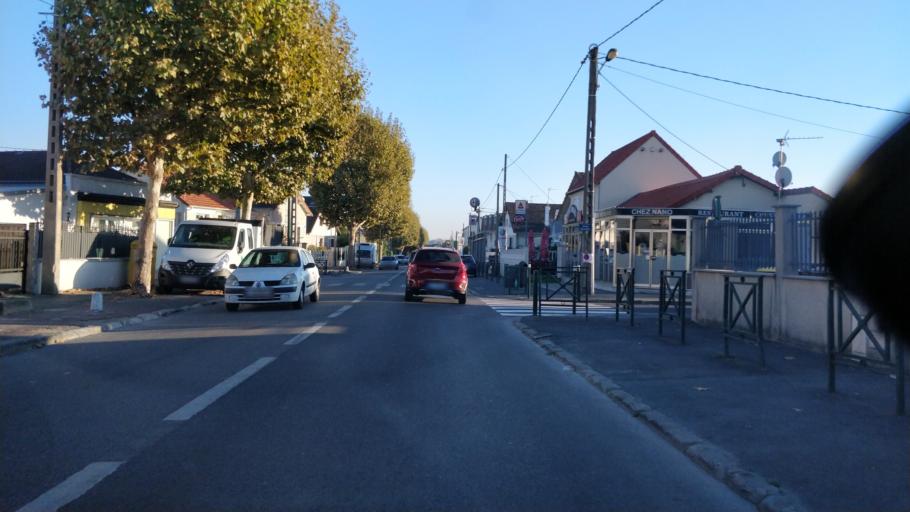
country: FR
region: Ile-de-France
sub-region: Departement de Seine-Saint-Denis
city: Neuilly-sur-Marne
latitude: 48.8726
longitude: 2.5536
